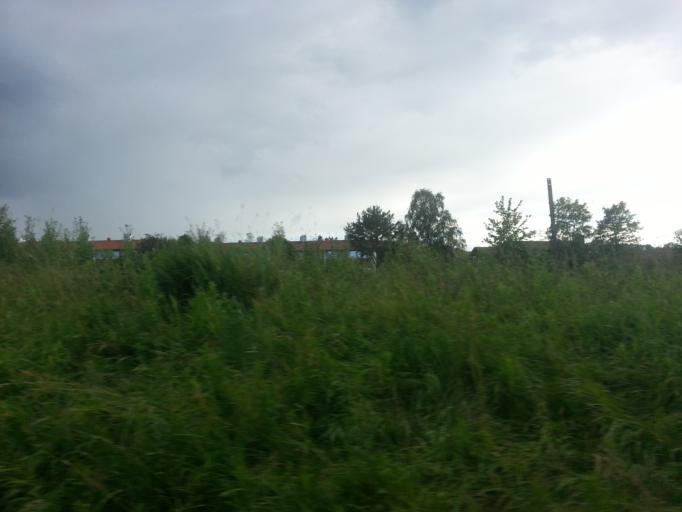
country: NO
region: Sor-Trondelag
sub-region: Trondheim
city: Trondheim
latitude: 63.4397
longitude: 10.4534
